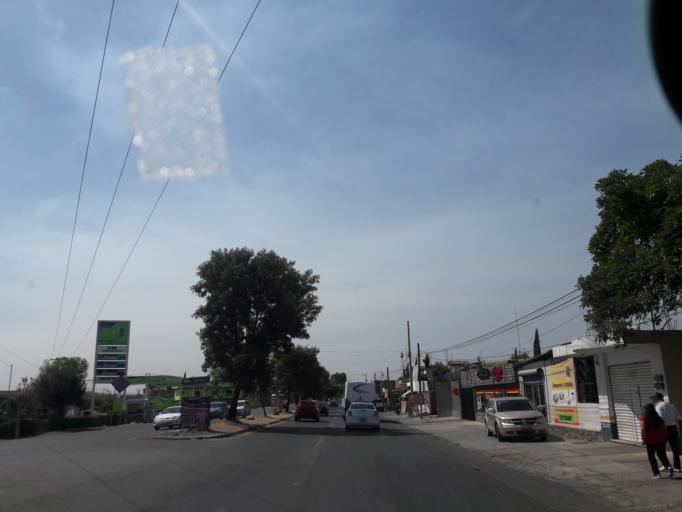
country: MX
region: Tlaxcala
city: Xiloxoxtla
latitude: 19.2629
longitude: -98.1994
